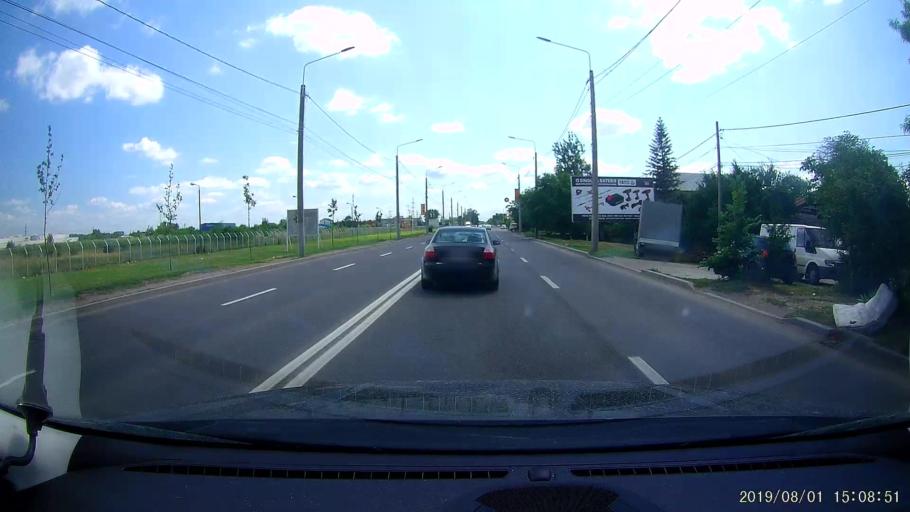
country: RO
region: Braila
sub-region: Municipiul Braila
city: Braila
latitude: 45.2382
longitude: 27.9425
